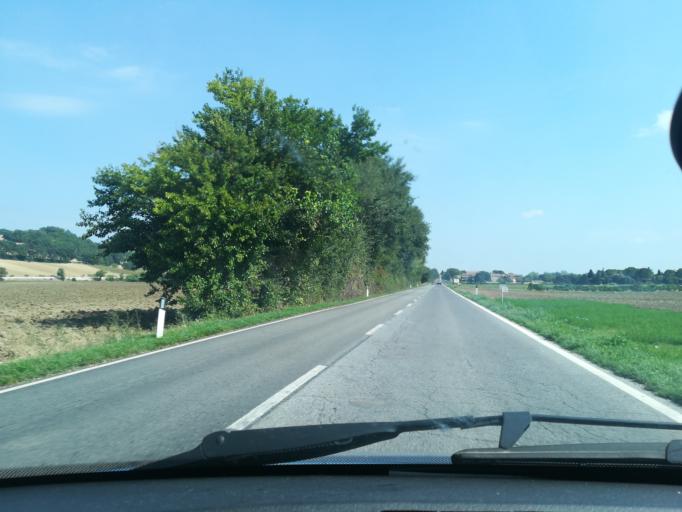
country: IT
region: The Marches
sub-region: Provincia di Macerata
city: Pollenza
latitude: 43.2352
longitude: 13.3587
